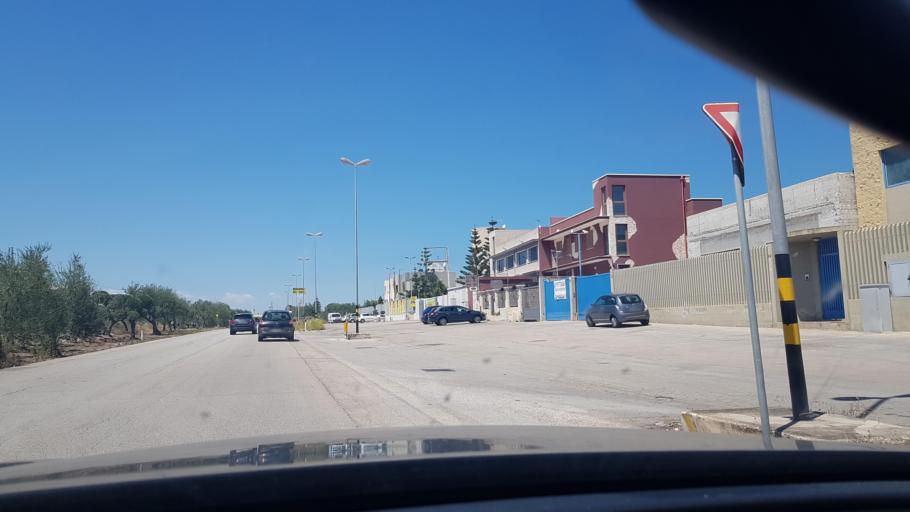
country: IT
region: Apulia
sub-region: Provincia di Barletta - Andria - Trani
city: Barletta
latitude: 41.3023
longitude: 16.3252
